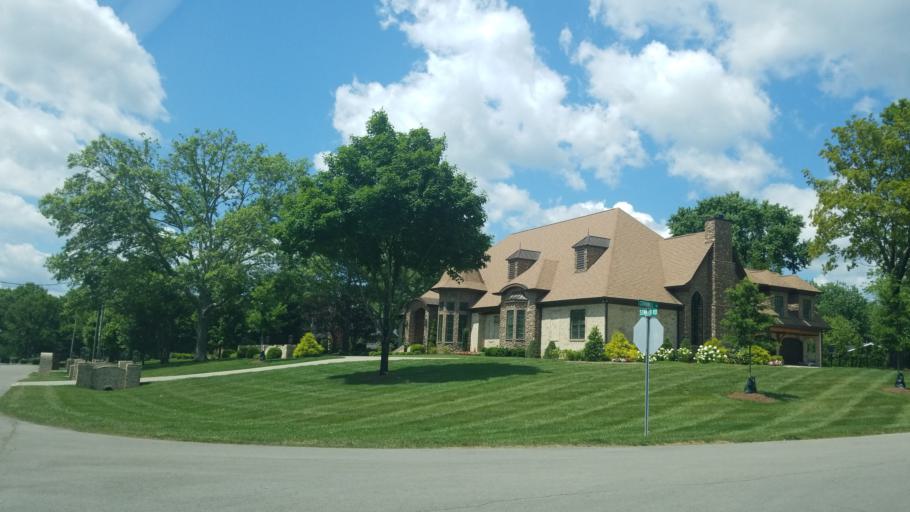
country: US
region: Tennessee
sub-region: Williamson County
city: Brentwood
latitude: 36.0278
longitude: -86.7974
